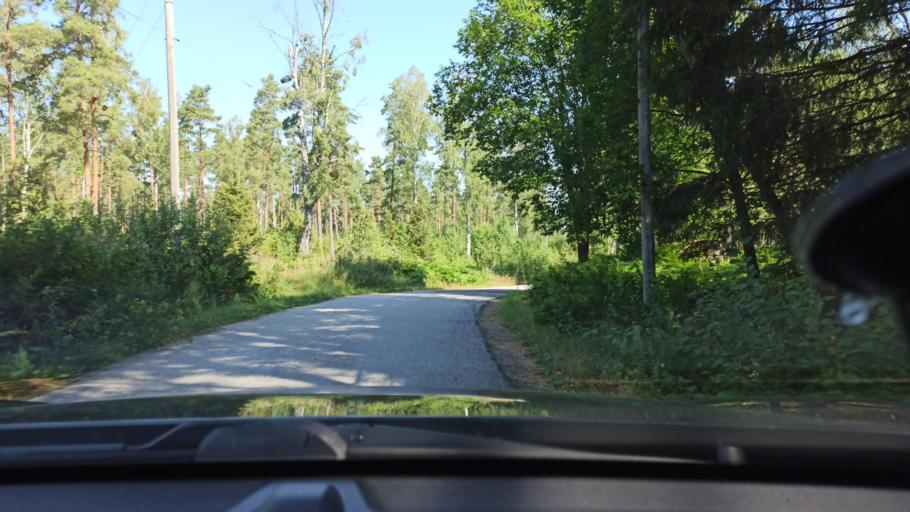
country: FI
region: Uusimaa
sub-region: Helsinki
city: Espoo
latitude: 60.1525
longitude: 24.5673
